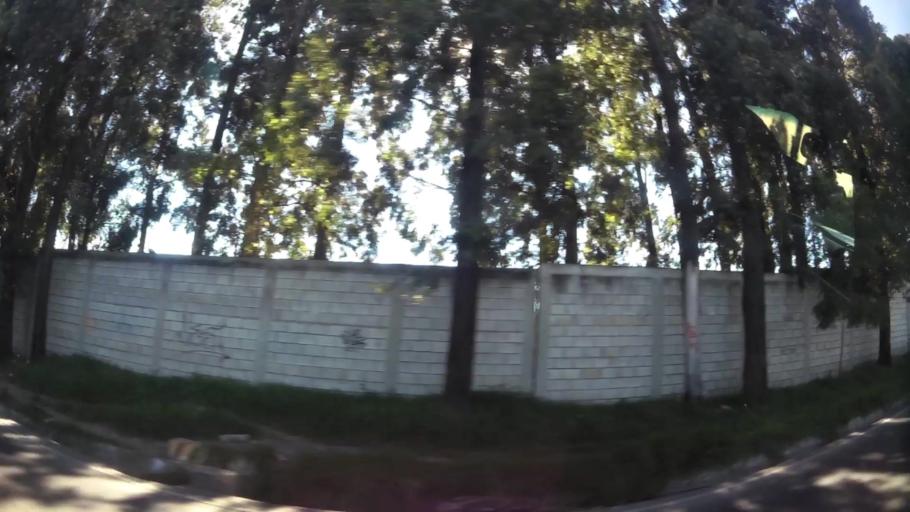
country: GT
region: Guatemala
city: Villa Nueva
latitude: 14.5378
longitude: -90.6062
